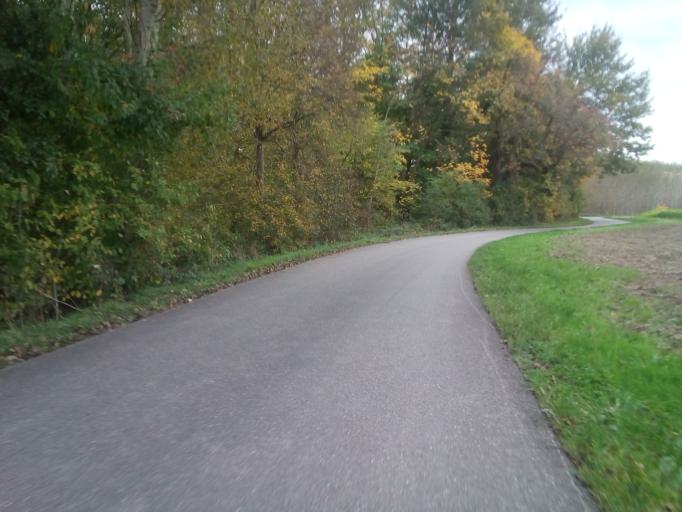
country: DE
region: Baden-Wuerttemberg
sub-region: Karlsruhe Region
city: Schwarzach
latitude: 48.7655
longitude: 8.0385
